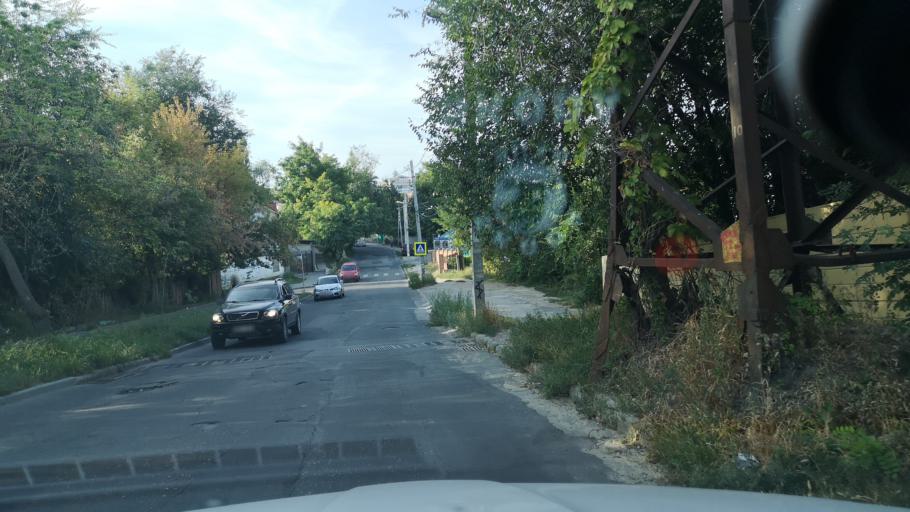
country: MD
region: Chisinau
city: Chisinau
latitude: 47.0099
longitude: 28.8481
